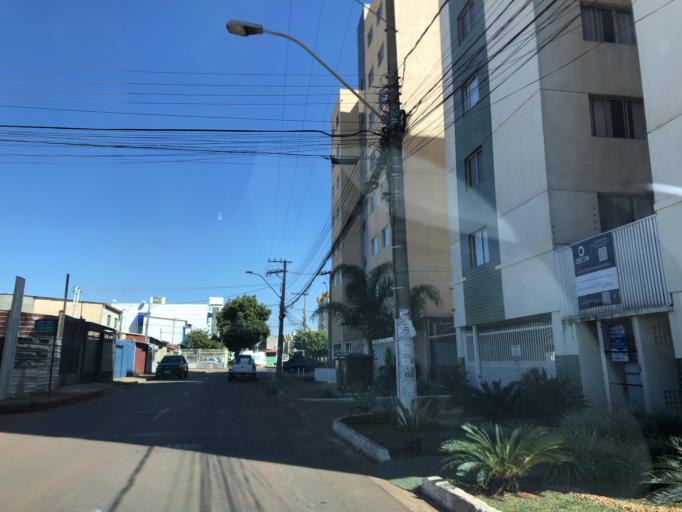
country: BR
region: Federal District
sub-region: Brasilia
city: Brasilia
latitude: -15.8669
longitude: -48.0622
